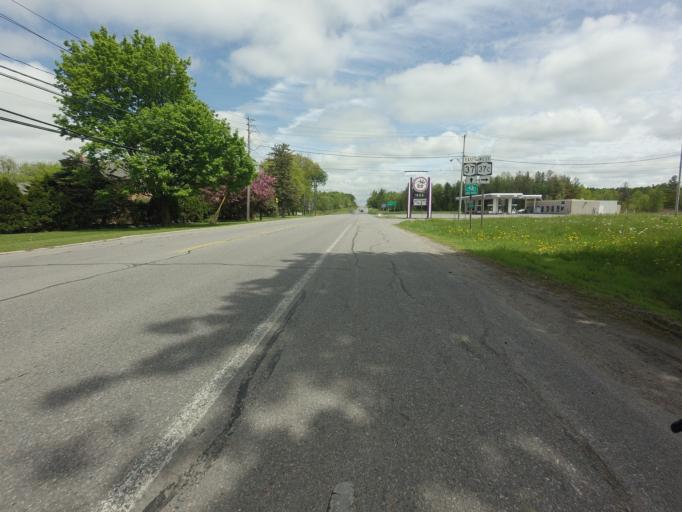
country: CA
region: Ontario
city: Cornwall
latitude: 44.9725
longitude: -74.6637
